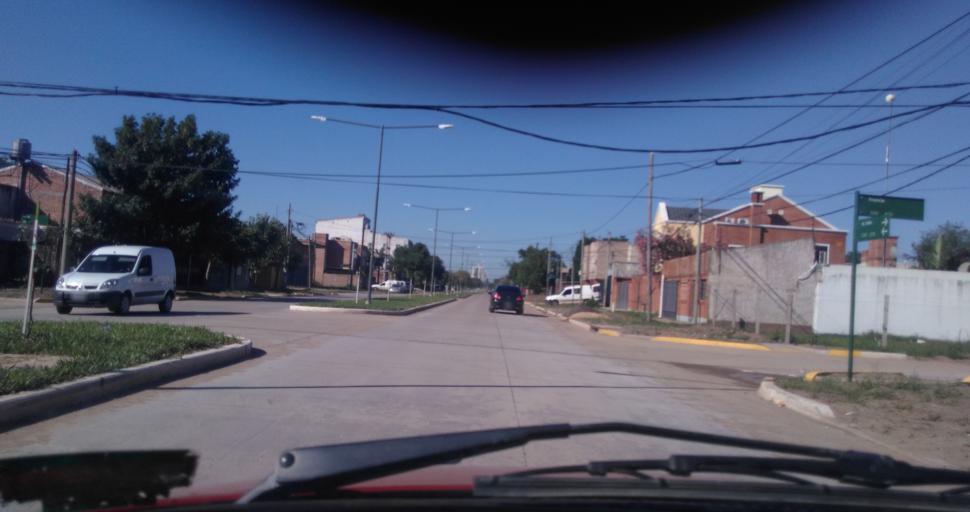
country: AR
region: Chaco
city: Resistencia
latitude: -27.4365
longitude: -58.9616
